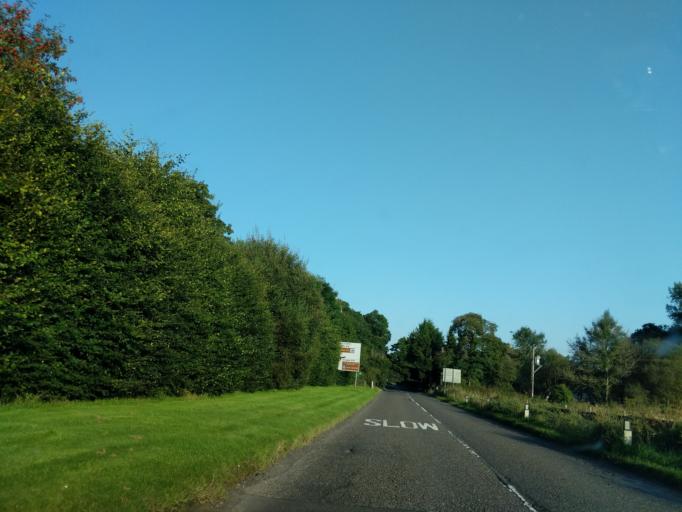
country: GB
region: Scotland
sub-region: Stirling
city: Balfron
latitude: 56.1730
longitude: -4.3690
